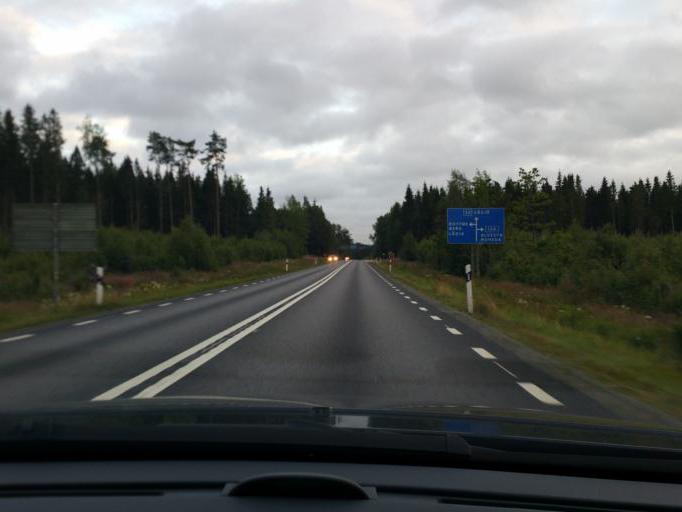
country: SE
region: Kronoberg
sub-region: Vaxjo Kommun
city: Lammhult
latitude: 57.0937
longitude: 14.6394
